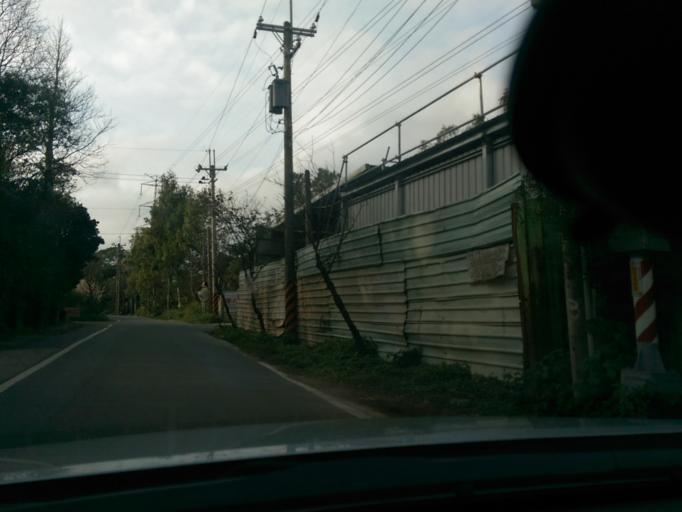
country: TW
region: Taiwan
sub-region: Taoyuan
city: Taoyuan
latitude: 25.0913
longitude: 121.3654
